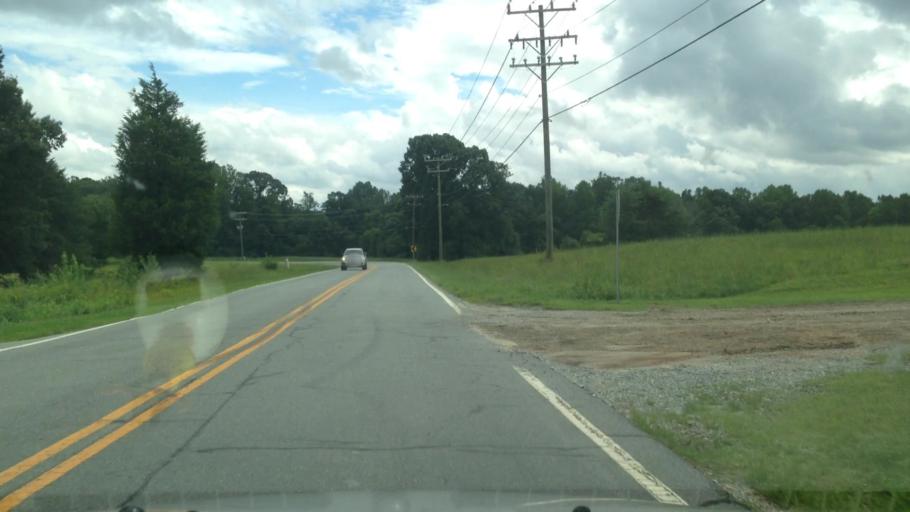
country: US
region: North Carolina
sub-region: Guilford County
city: Oak Ridge
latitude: 36.1946
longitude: -80.0606
